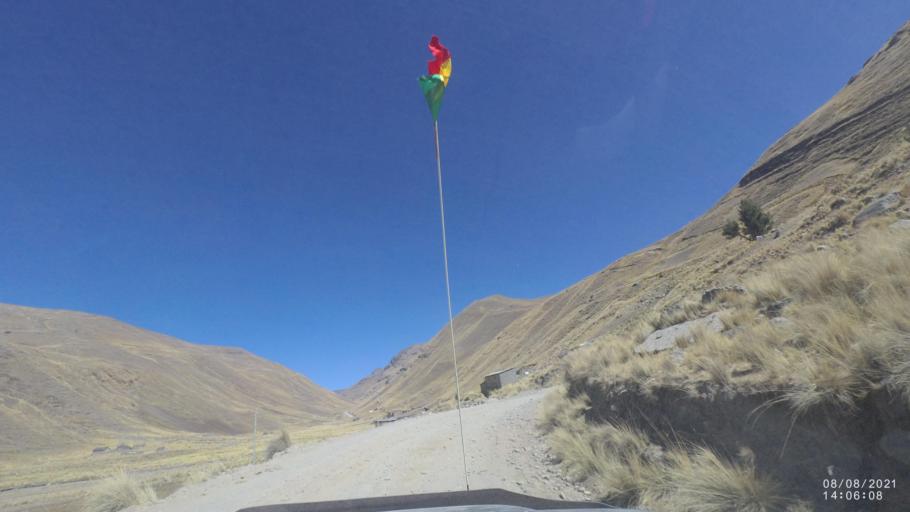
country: BO
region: Cochabamba
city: Sipe Sipe
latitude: -17.1222
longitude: -66.4412
